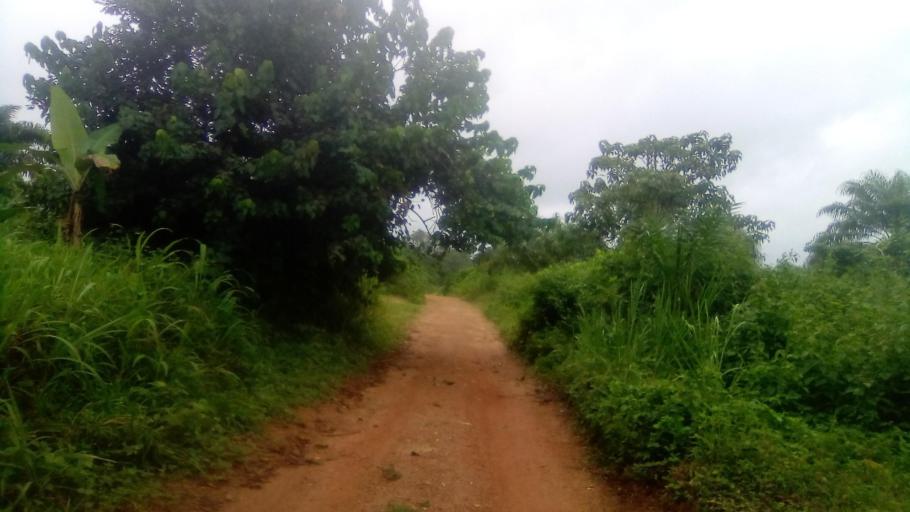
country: SL
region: Eastern Province
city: Kailahun
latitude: 8.2953
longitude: -10.5550
